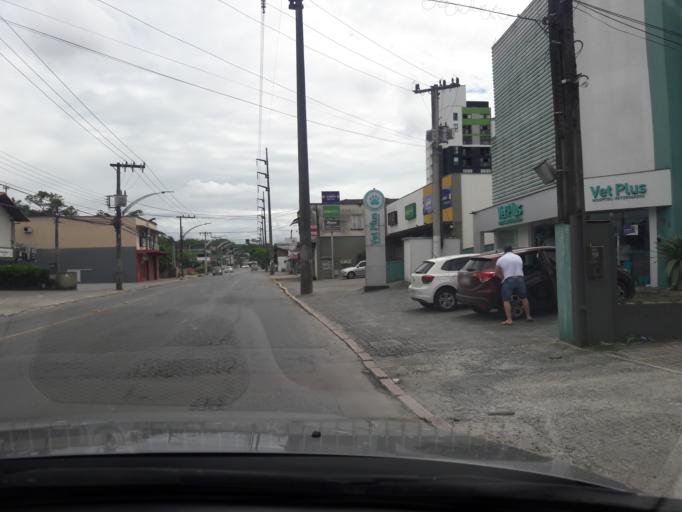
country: BR
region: Santa Catarina
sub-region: Joinville
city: Joinville
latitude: -26.3208
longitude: -48.8522
